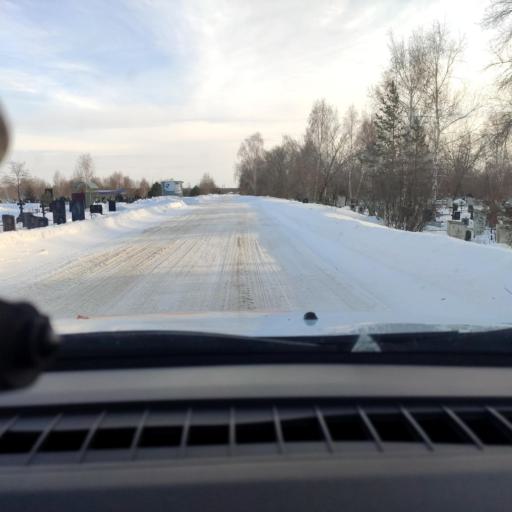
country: RU
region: Samara
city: Chapayevsk
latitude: 52.9897
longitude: 49.7451
